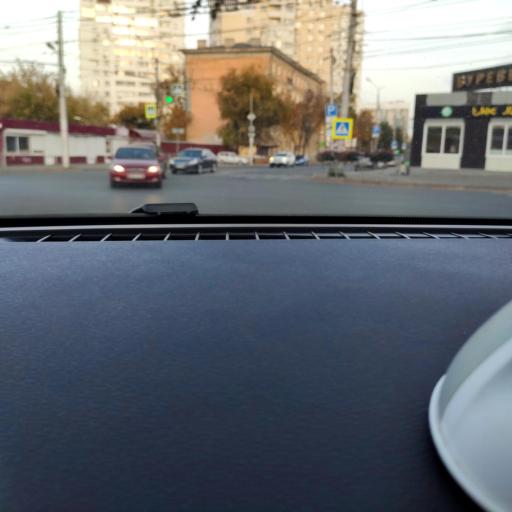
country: RU
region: Samara
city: Samara
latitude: 53.1956
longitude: 50.1252
